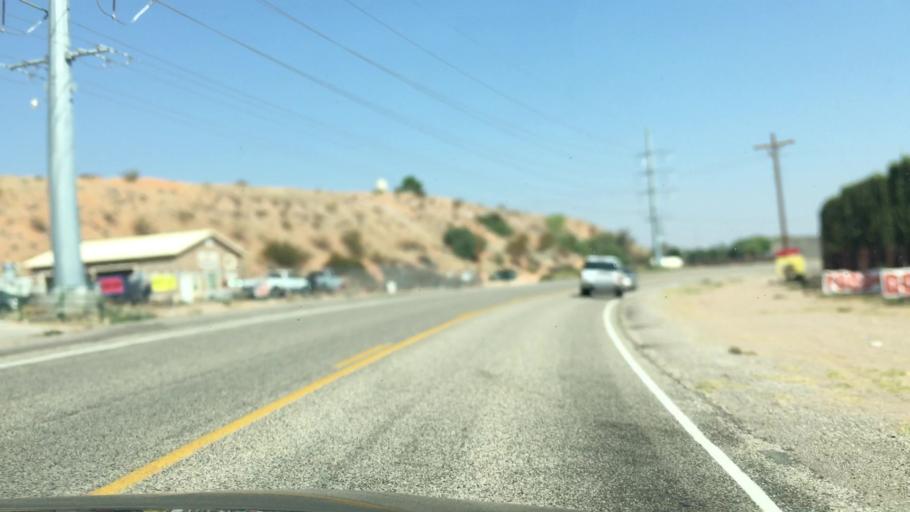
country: US
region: Arizona
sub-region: Mohave County
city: Beaver Dam
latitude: 36.8976
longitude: -113.9340
